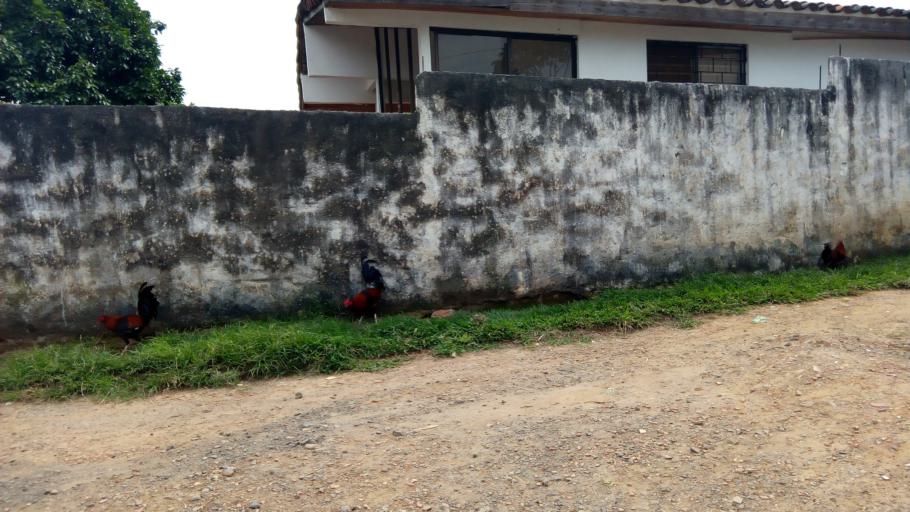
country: CO
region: Valle del Cauca
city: Cali
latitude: 3.3856
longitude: -76.5660
